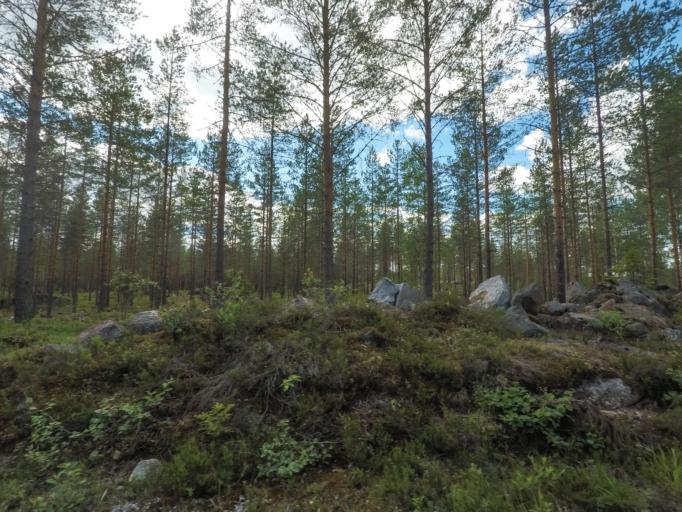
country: FI
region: Central Finland
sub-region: Jyvaeskylae
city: Hankasalmi
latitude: 62.4053
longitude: 26.6583
